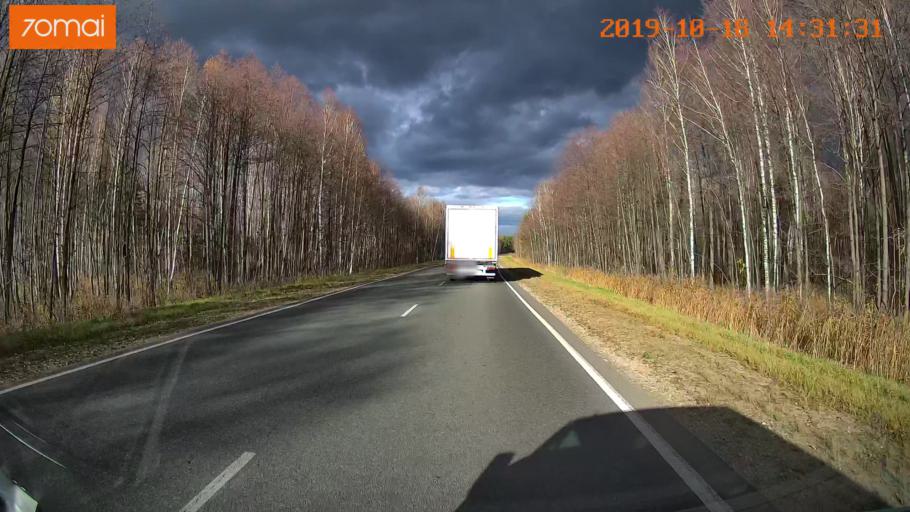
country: RU
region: Rjazan
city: Tuma
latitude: 55.1835
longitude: 40.5705
